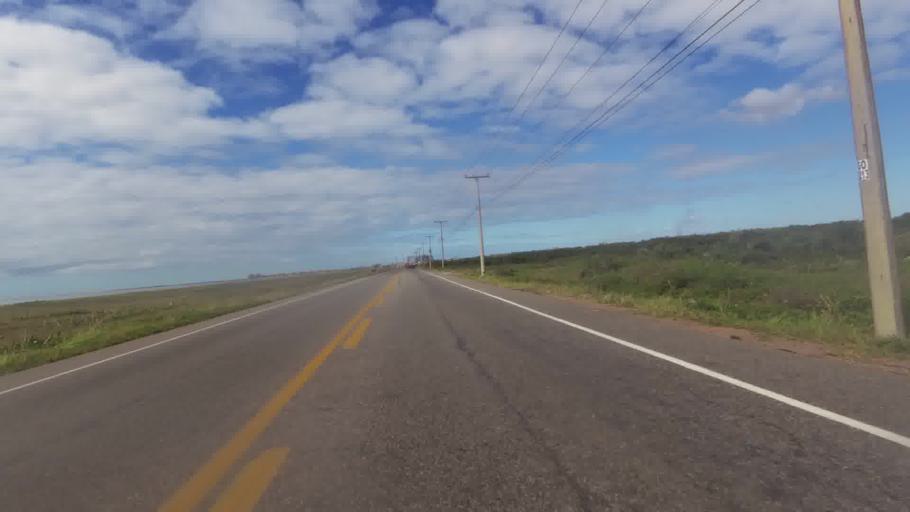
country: BR
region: Espirito Santo
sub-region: Itapemirim
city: Itapemirim
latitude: -20.9801
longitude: -40.8117
